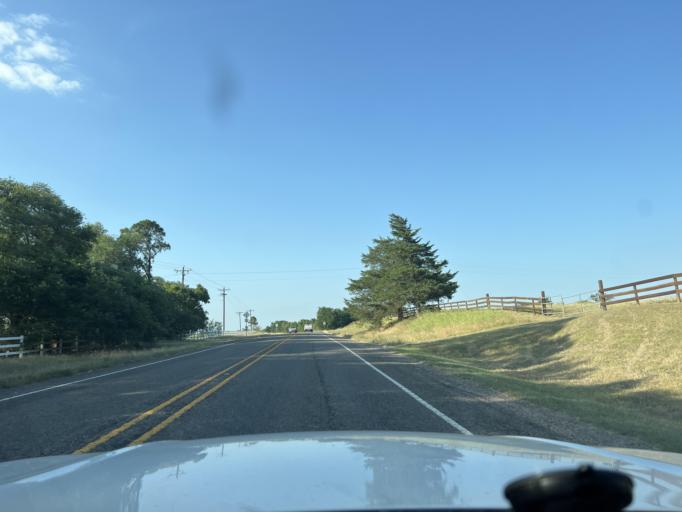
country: US
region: Texas
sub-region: Washington County
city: Brenham
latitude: 30.1513
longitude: -96.2571
